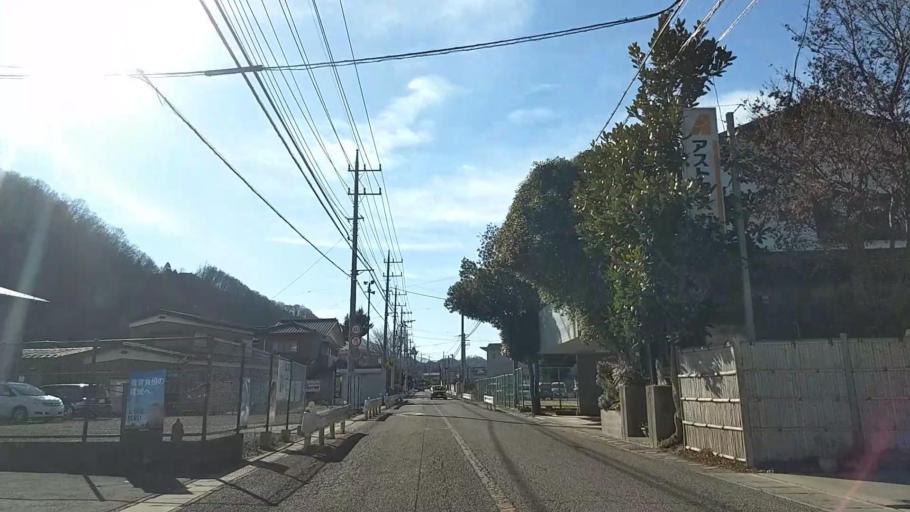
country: JP
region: Yamanashi
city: Otsuki
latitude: 35.5724
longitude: 138.9266
